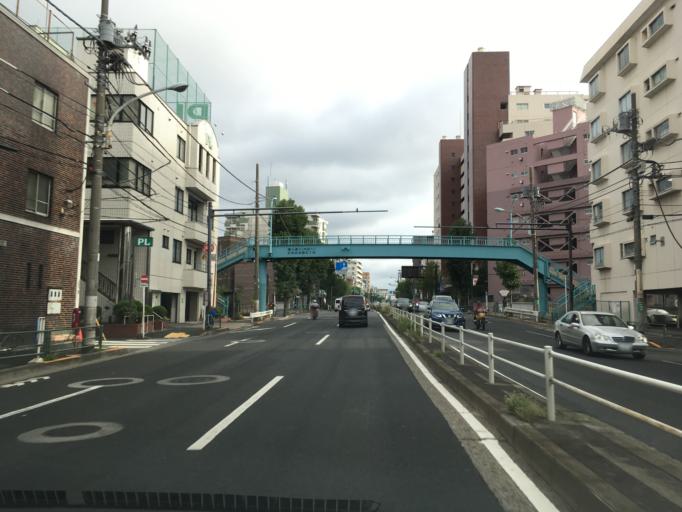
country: JP
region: Tokyo
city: Musashino
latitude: 35.7019
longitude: 139.6167
